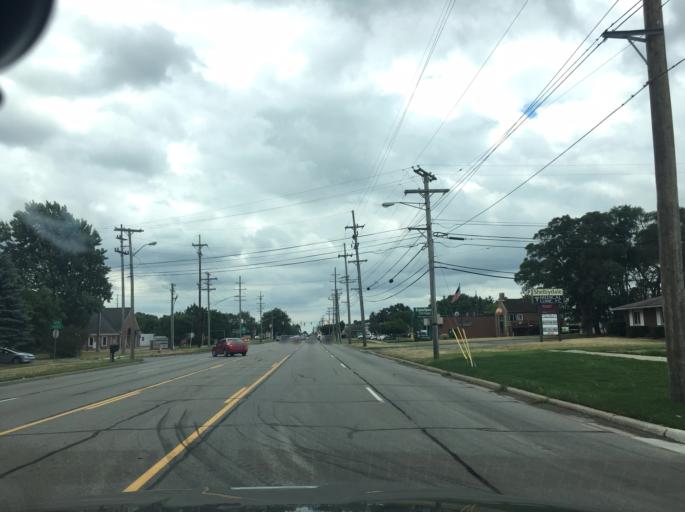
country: US
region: Michigan
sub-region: Macomb County
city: Shelby
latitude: 42.6572
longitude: -83.0335
